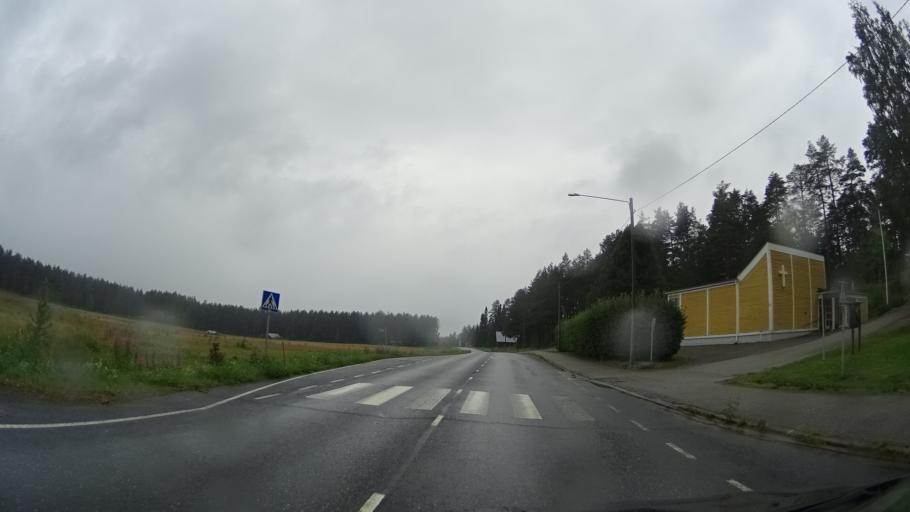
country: FI
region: North Karelia
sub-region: Keski-Karjala
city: Raeaekkylae
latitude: 62.3155
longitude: 29.6193
